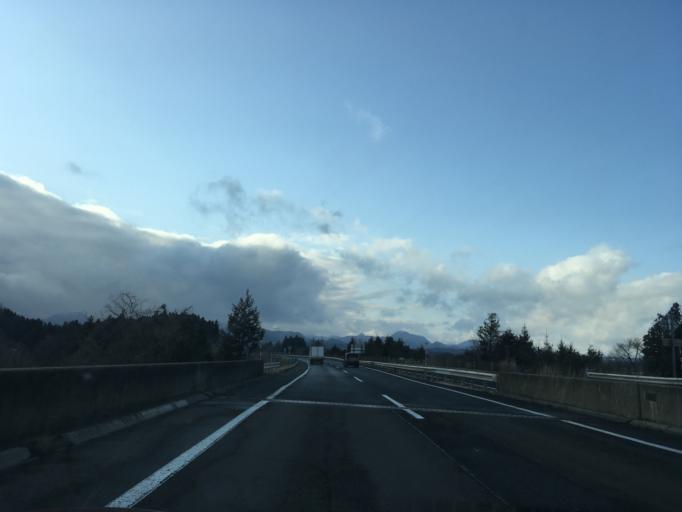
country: JP
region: Miyagi
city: Okawara
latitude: 38.1688
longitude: 140.6387
